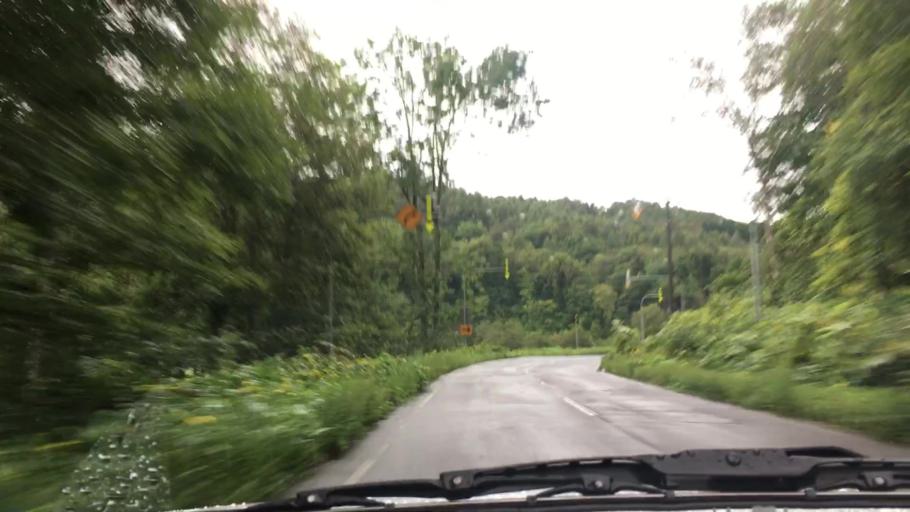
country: JP
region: Hokkaido
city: Niseko Town
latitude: 42.6638
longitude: 140.7772
